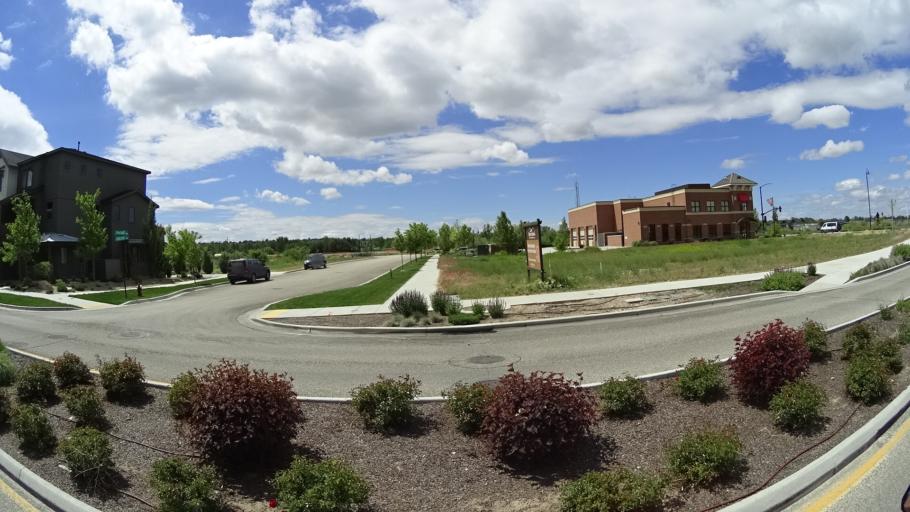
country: US
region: Idaho
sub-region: Ada County
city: Boise
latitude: 43.5762
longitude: -116.1388
